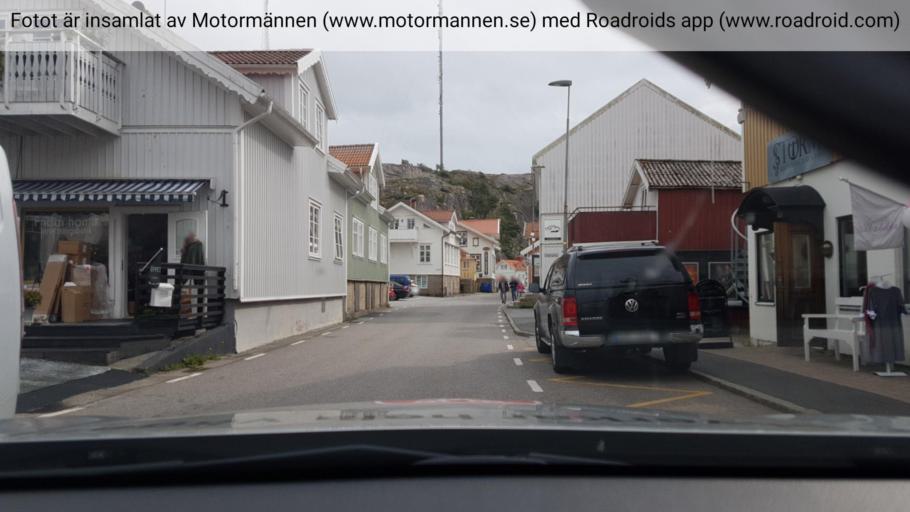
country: SE
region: Vaestra Goetaland
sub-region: Tanums Kommun
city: Grebbestad
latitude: 58.6906
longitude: 11.2562
